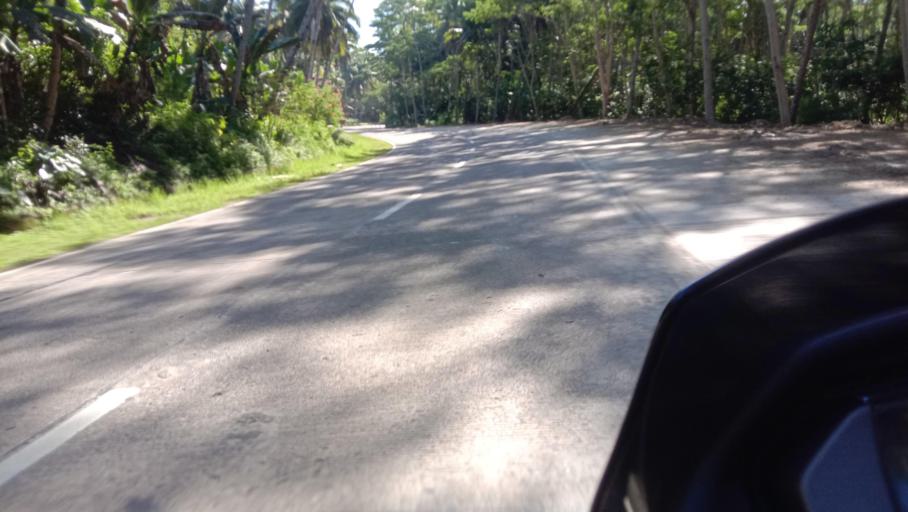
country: PH
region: Caraga
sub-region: Province of Surigao del Sur
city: Amaga
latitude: 8.5357
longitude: 126.0861
